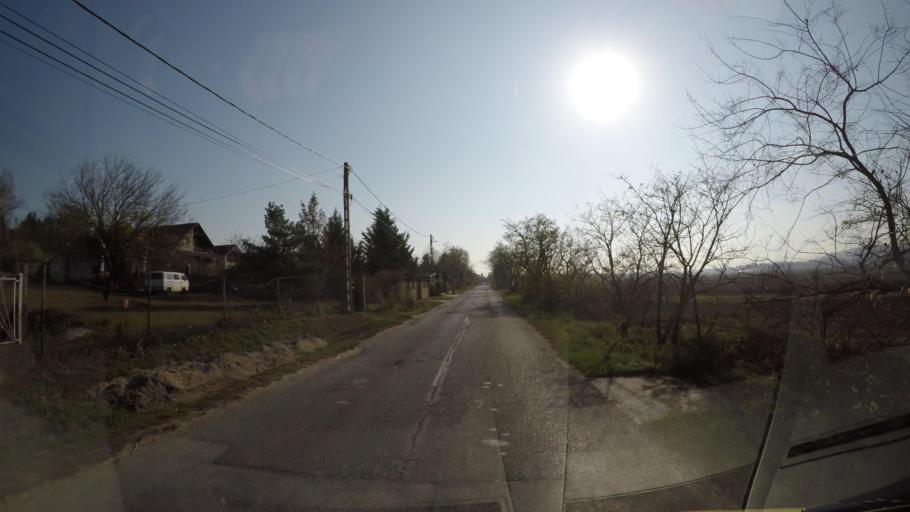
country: HU
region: Pest
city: Leanyfalu
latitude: 47.7094
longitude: 19.1068
